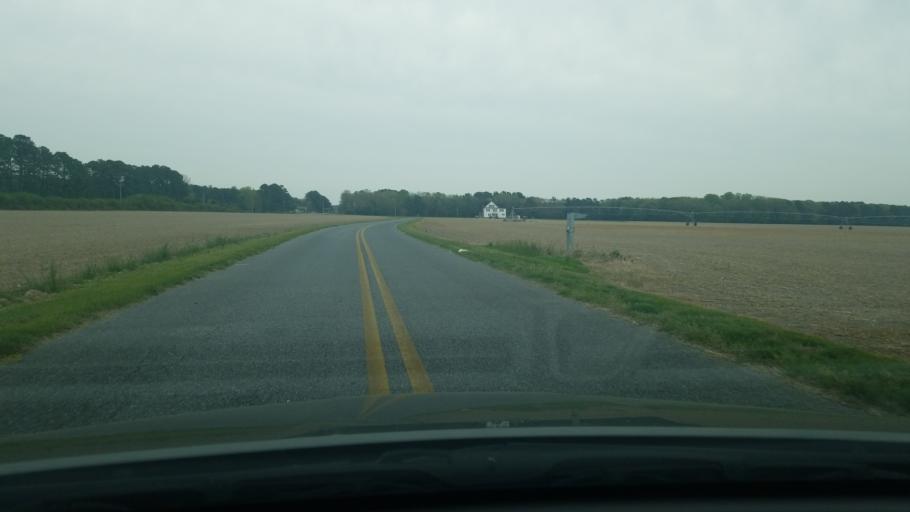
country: US
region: Maryland
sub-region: Worcester County
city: Snow Hill
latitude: 38.2376
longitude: -75.3071
